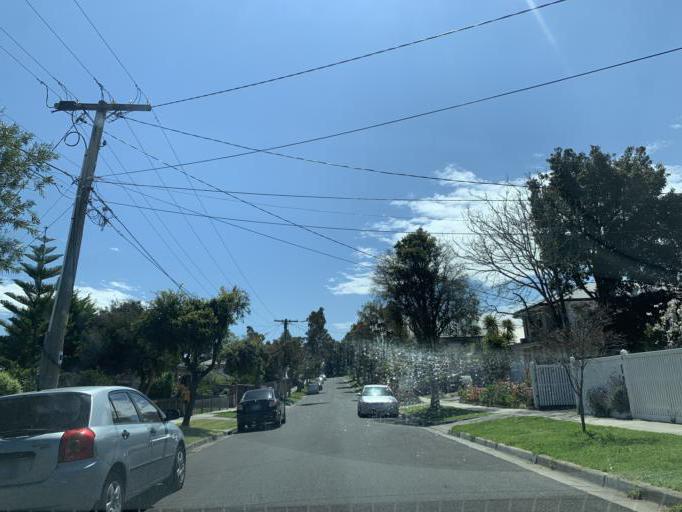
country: AU
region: Victoria
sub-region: Bayside
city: Highett
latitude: -37.9461
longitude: 145.0365
